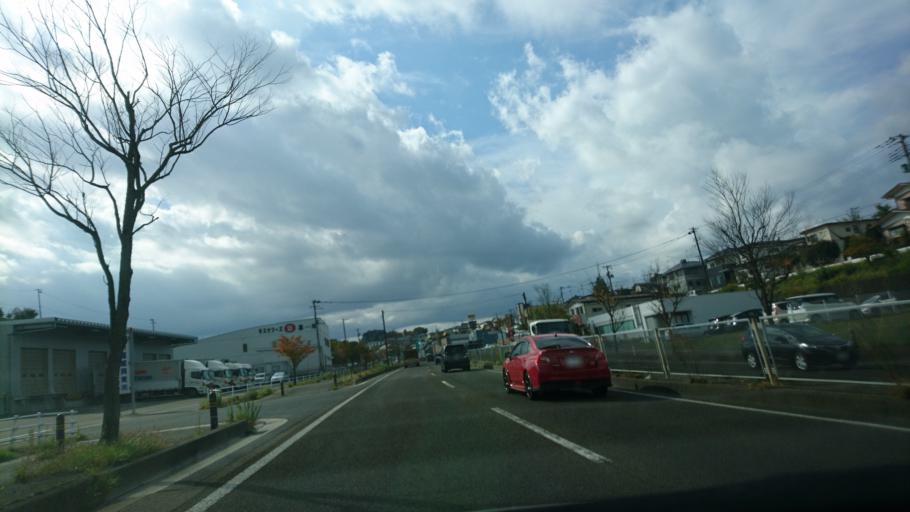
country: JP
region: Miyagi
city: Tomiya
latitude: 38.3679
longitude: 140.8739
